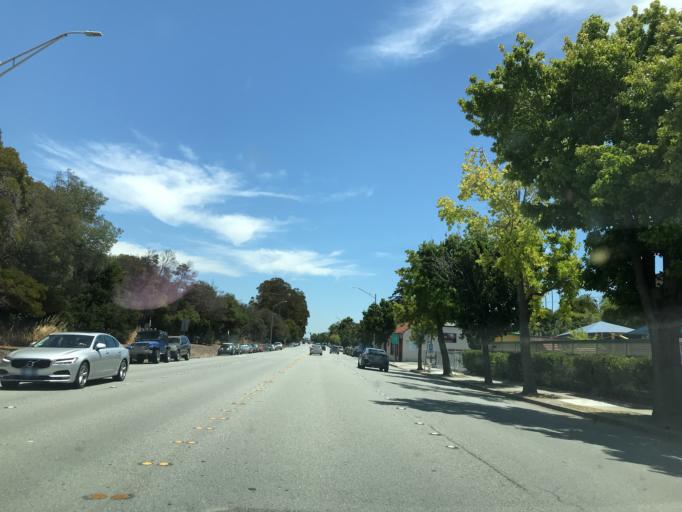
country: US
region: California
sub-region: San Mateo County
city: Burlingame
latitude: 37.5858
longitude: -122.3594
